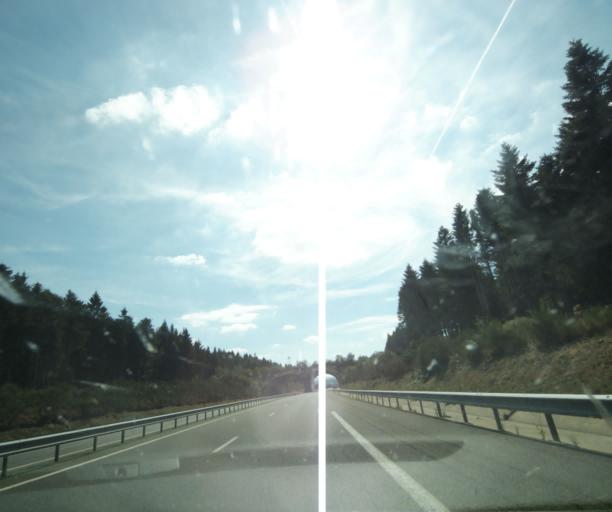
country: FR
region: Auvergne
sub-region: Departement du Puy-de-Dome
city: Gelles
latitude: 45.7074
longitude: 2.6963
